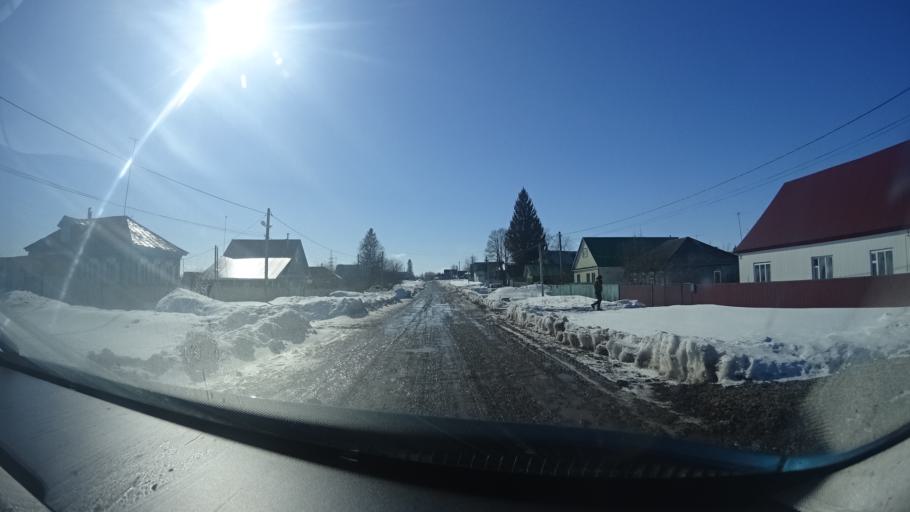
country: RU
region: Bashkortostan
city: Chishmy
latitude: 54.5802
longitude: 55.3822
